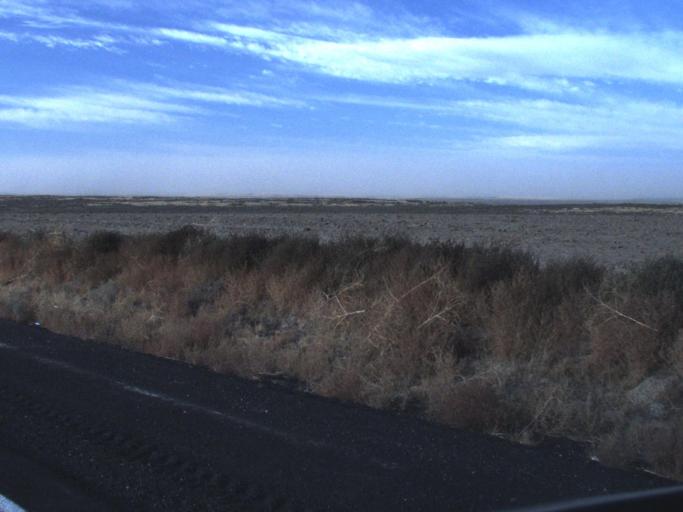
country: US
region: Washington
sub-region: Grant County
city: Warden
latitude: 47.3518
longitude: -118.9395
